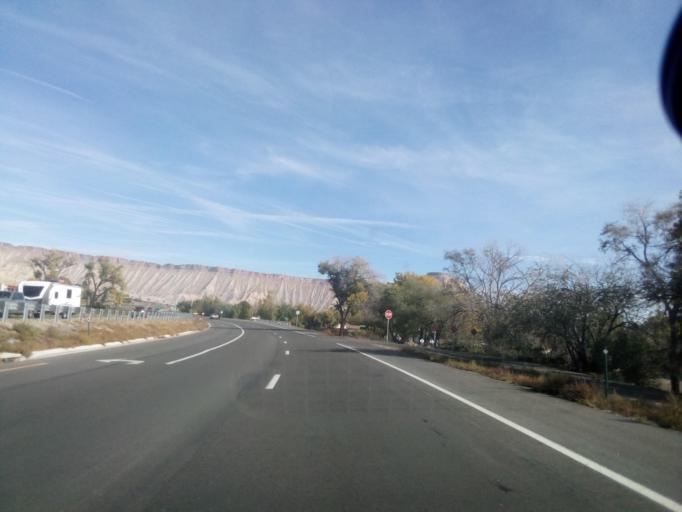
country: US
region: Colorado
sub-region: Mesa County
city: Clifton
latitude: 39.0949
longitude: -108.4506
